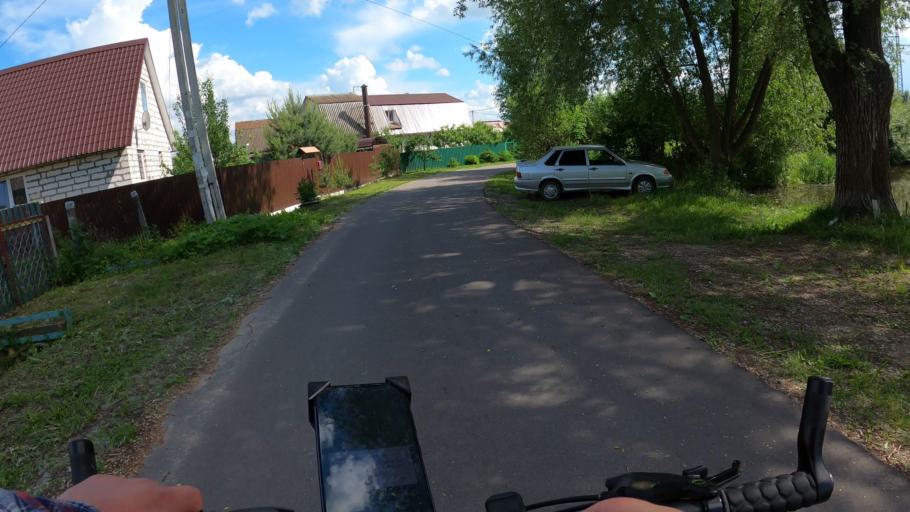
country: RU
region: Moskovskaya
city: Konobeyevo
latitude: 55.3932
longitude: 38.6832
